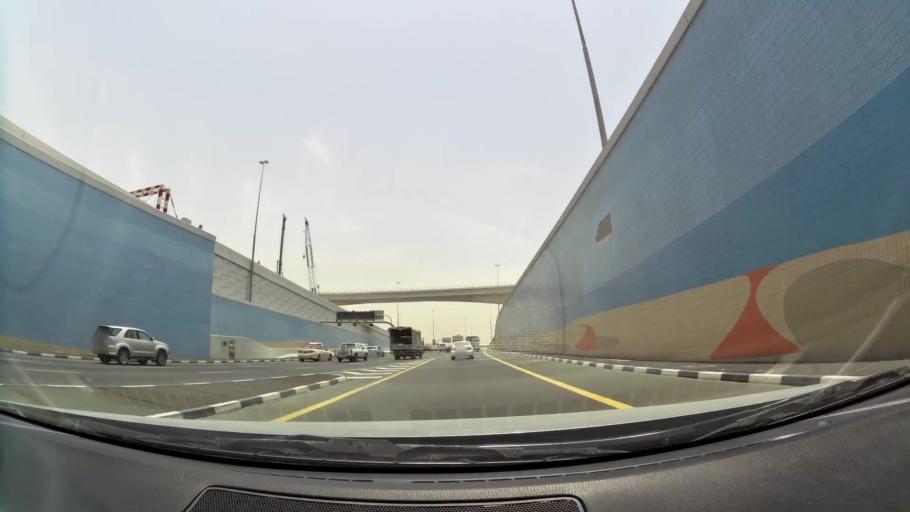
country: AE
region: Ash Shariqah
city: Sharjah
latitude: 25.2365
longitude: 55.3776
